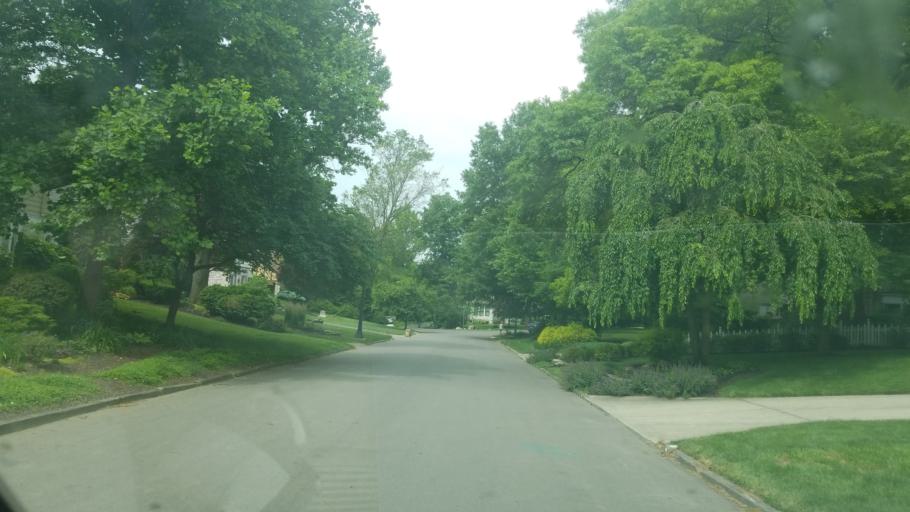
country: US
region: Ohio
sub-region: Franklin County
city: Worthington
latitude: 40.0403
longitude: -83.0226
